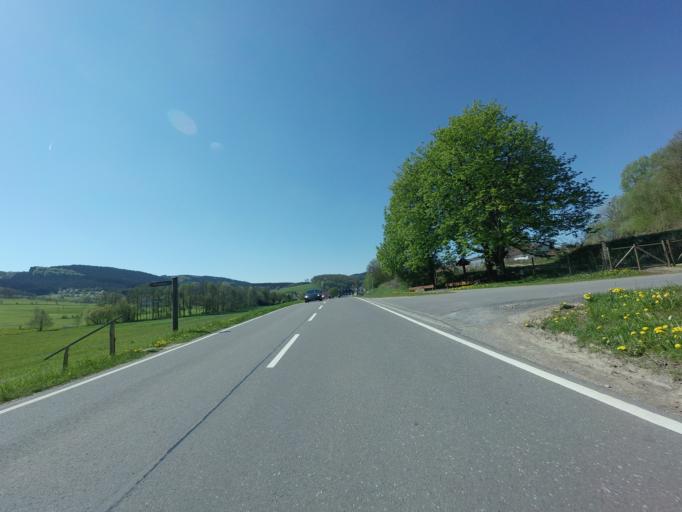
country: DE
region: North Rhine-Westphalia
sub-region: Regierungsbezirk Arnsberg
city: Finnentrop
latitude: 51.1092
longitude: 7.9587
